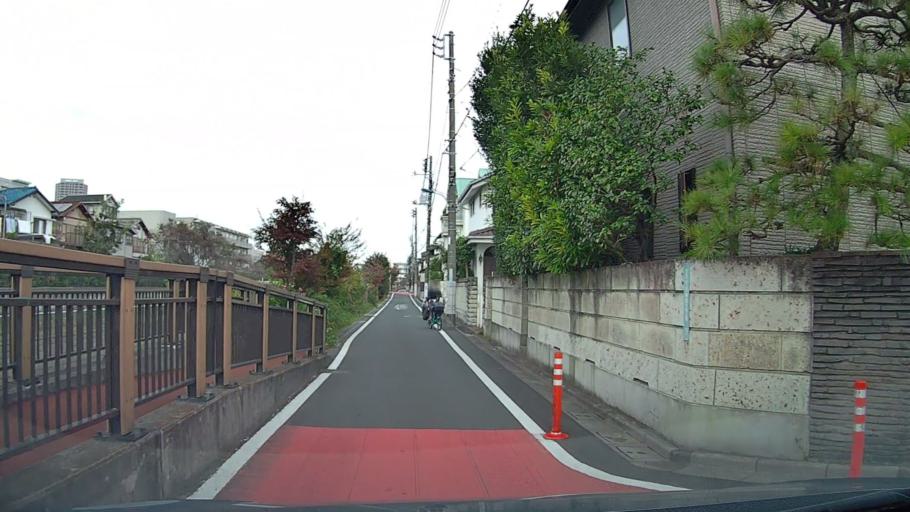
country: JP
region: Saitama
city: Wako
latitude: 35.7374
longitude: 139.6063
